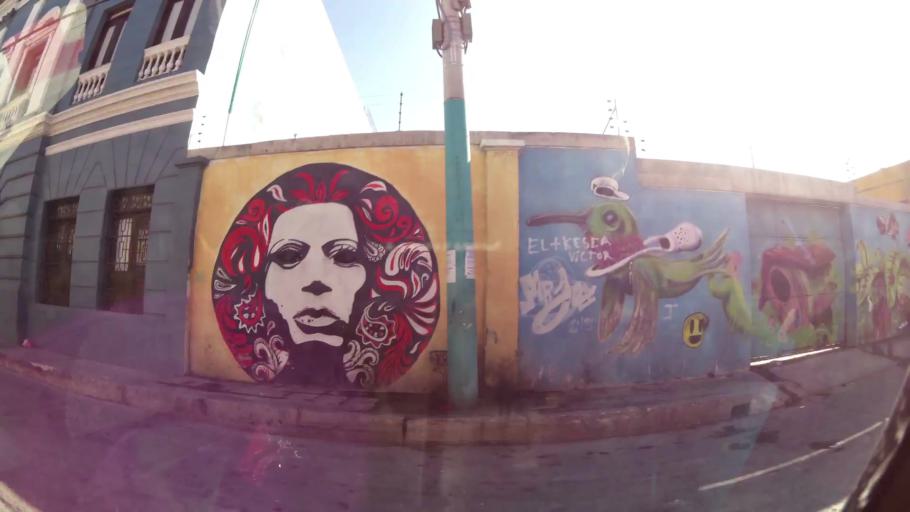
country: CO
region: Atlantico
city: Barranquilla
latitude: 10.9786
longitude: -74.7803
